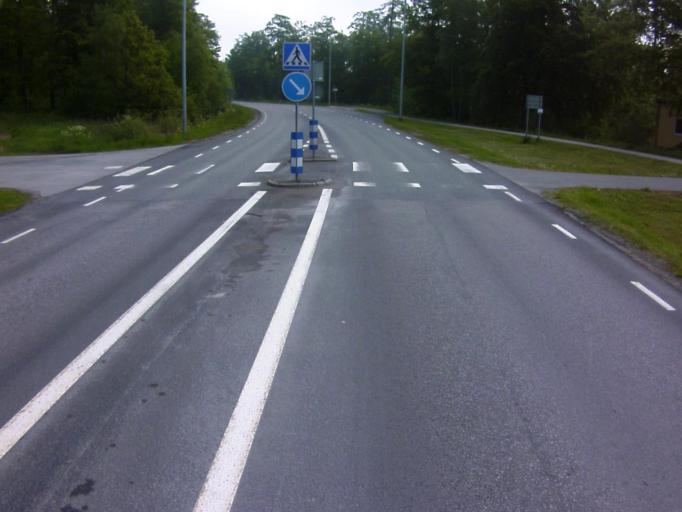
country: SE
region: Blekinge
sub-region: Solvesborgs Kommun
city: Soelvesborg
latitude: 56.0543
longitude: 14.5694
